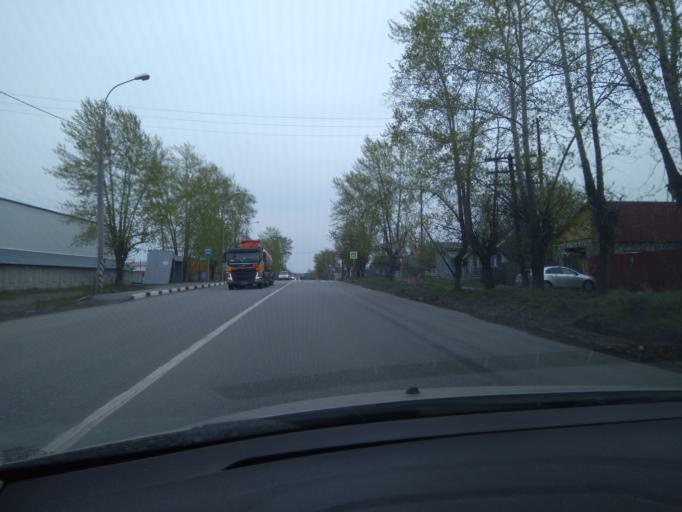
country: RU
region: Sverdlovsk
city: Beloyarskiy
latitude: 56.7567
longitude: 61.3568
